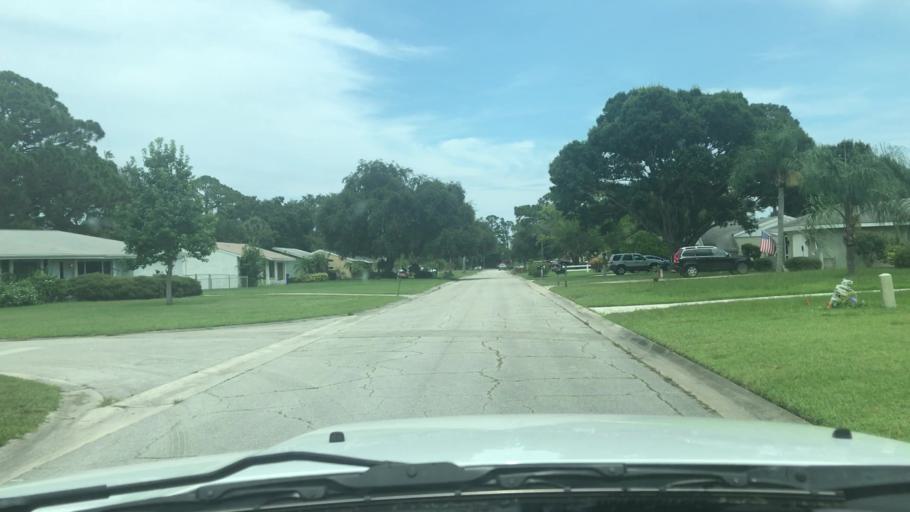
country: US
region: Florida
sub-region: Indian River County
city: Florida Ridge
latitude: 27.5588
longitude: -80.3849
